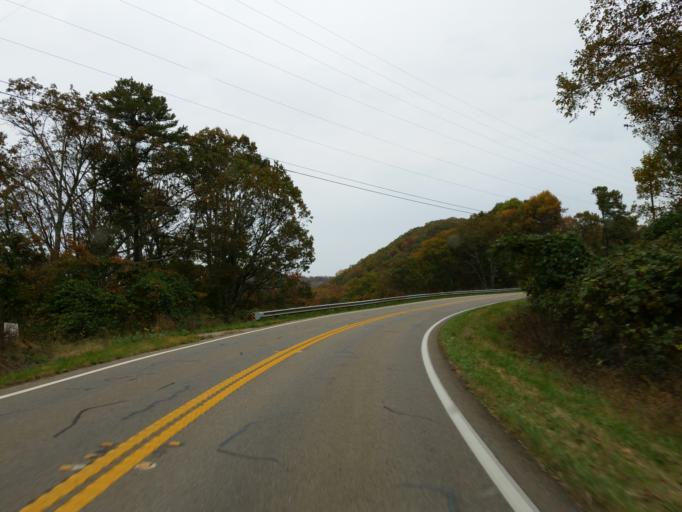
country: US
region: Georgia
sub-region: Pickens County
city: Jasper
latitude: 34.5308
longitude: -84.4140
